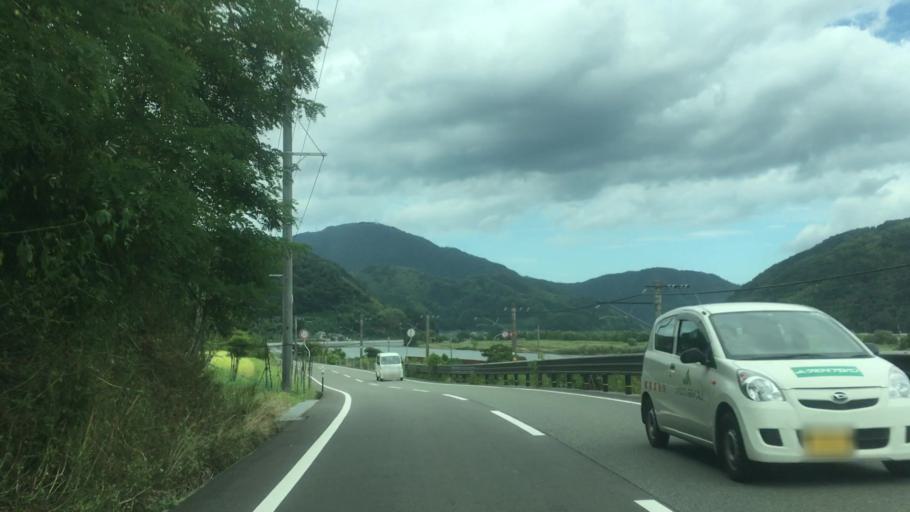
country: JP
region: Hyogo
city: Toyooka
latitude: 35.5746
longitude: 134.8048
